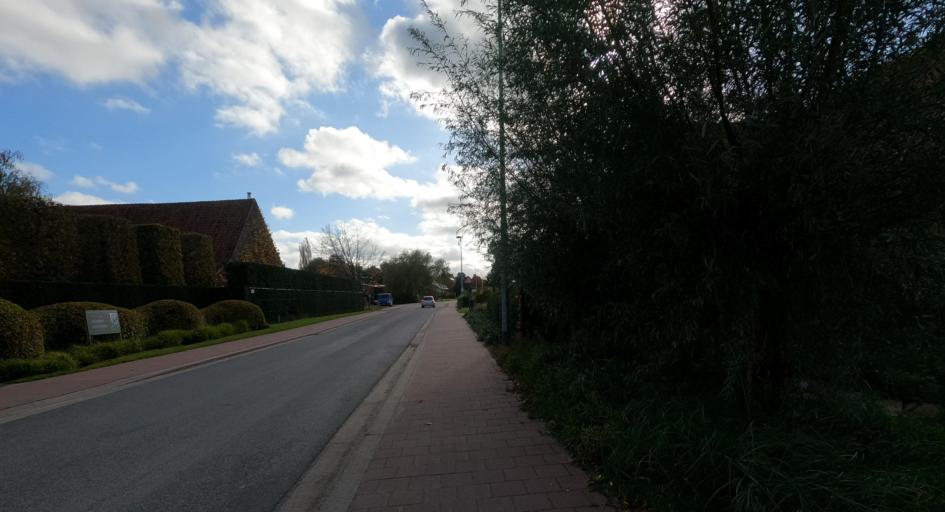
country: BE
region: Flanders
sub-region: Provincie Antwerpen
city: Wuustwezel
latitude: 51.3653
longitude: 4.5446
